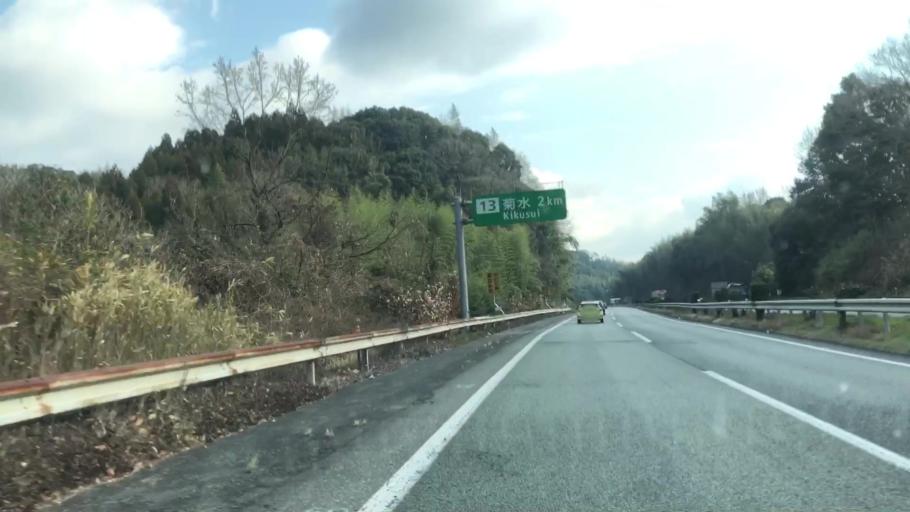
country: JP
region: Kumamoto
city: Tamana
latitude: 33.0003
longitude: 130.5903
